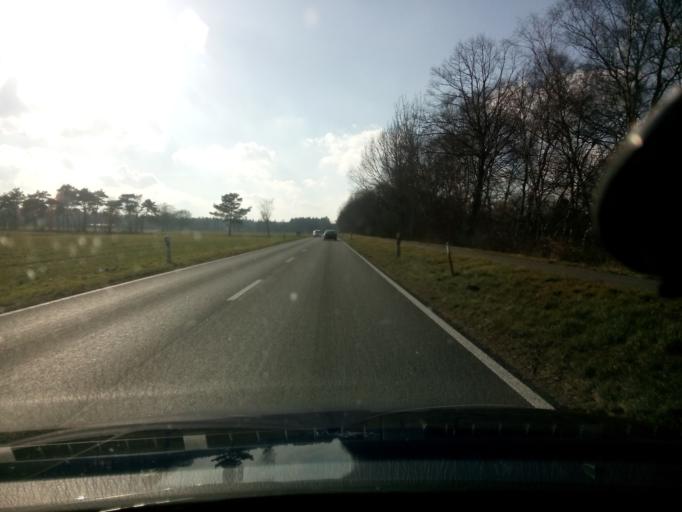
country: DE
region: Lower Saxony
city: Worpswede
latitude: 53.2104
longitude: 8.8896
